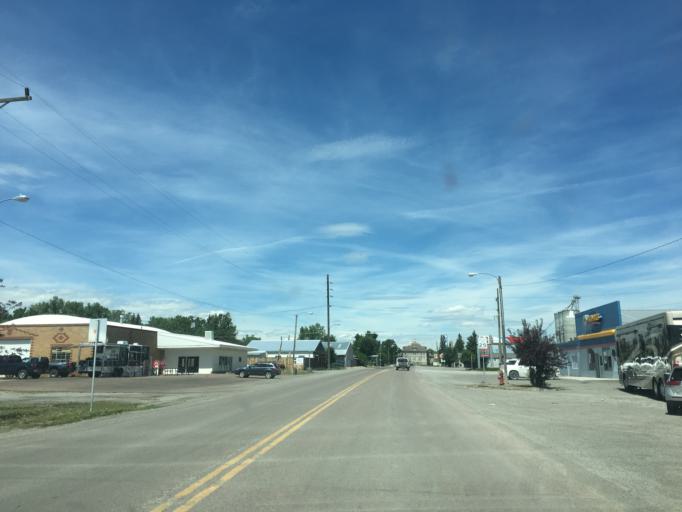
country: US
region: Montana
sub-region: Teton County
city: Choteau
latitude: 47.8074
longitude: -112.1793
